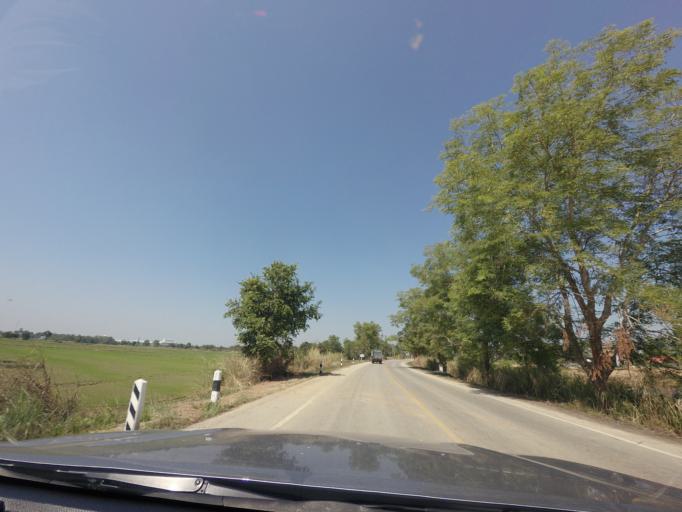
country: TH
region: Sukhothai
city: Si Samrong
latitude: 17.1095
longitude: 99.7779
